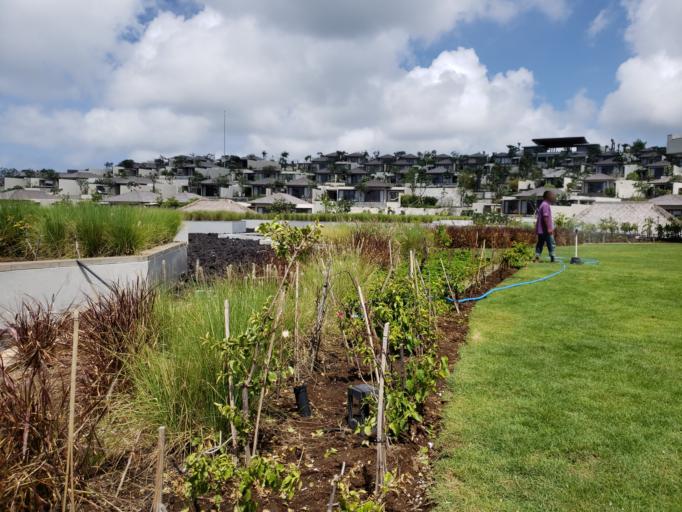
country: ID
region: Bali
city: Kangin
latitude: -8.8462
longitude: 115.1309
